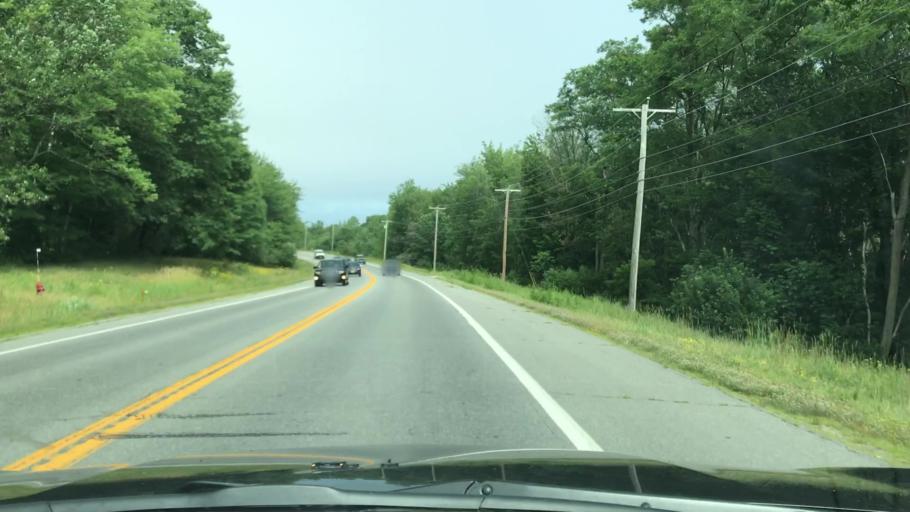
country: US
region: Maine
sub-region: Waldo County
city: Belfast
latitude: 44.4356
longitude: -68.9441
